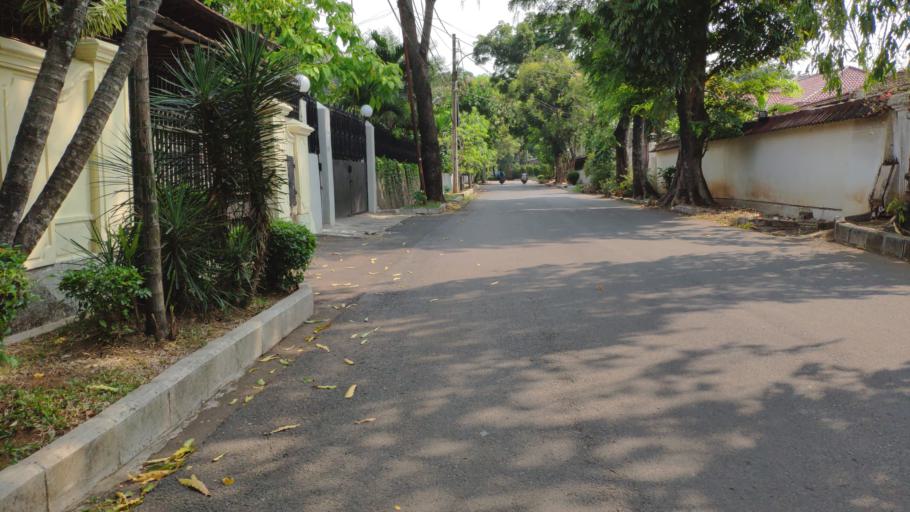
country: ID
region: Jakarta Raya
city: Jakarta
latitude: -6.2673
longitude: 106.8197
